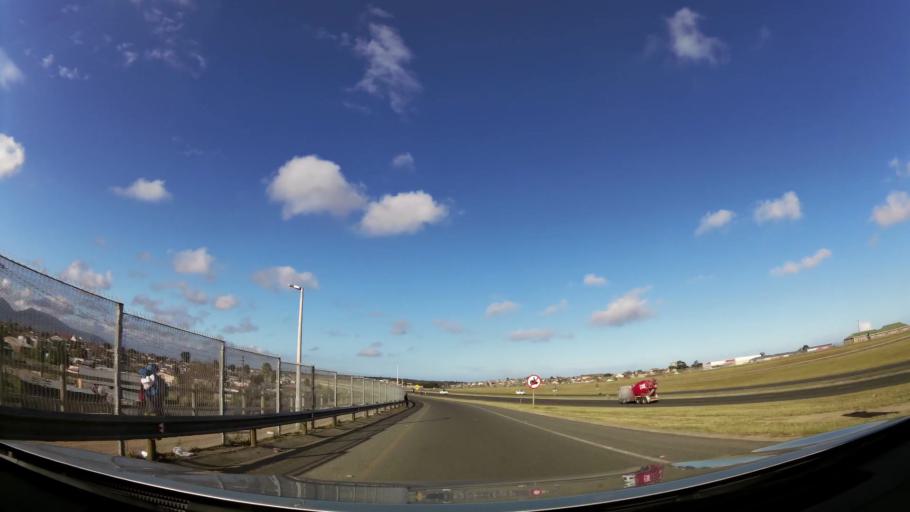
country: ZA
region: Western Cape
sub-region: Eden District Municipality
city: George
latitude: -33.9953
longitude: 22.4766
